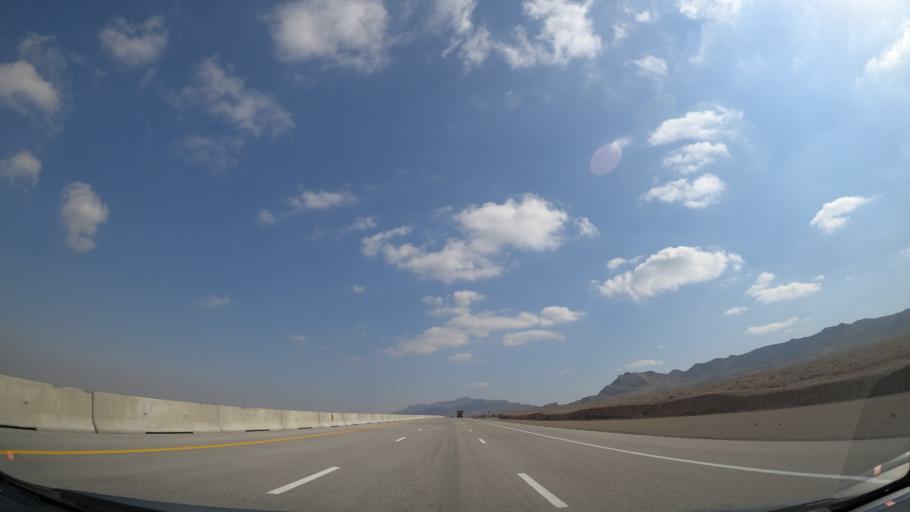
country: IR
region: Alborz
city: Eshtehard
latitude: 35.7101
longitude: 50.5976
